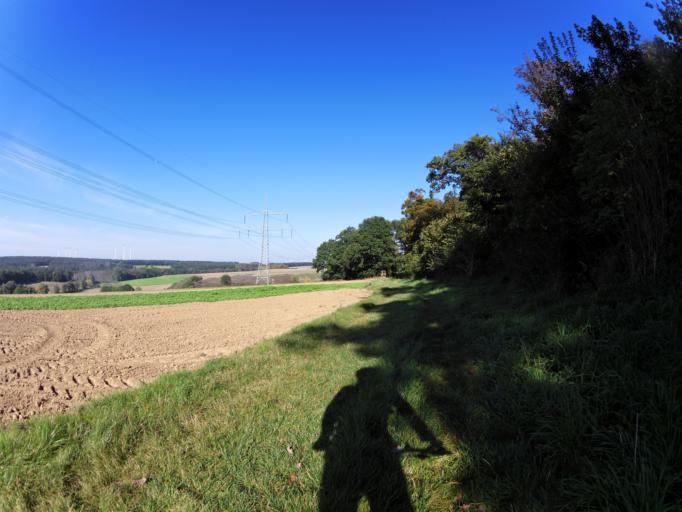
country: DE
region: Bavaria
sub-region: Regierungsbezirk Unterfranken
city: Ochsenfurt
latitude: 49.6875
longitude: 10.0605
